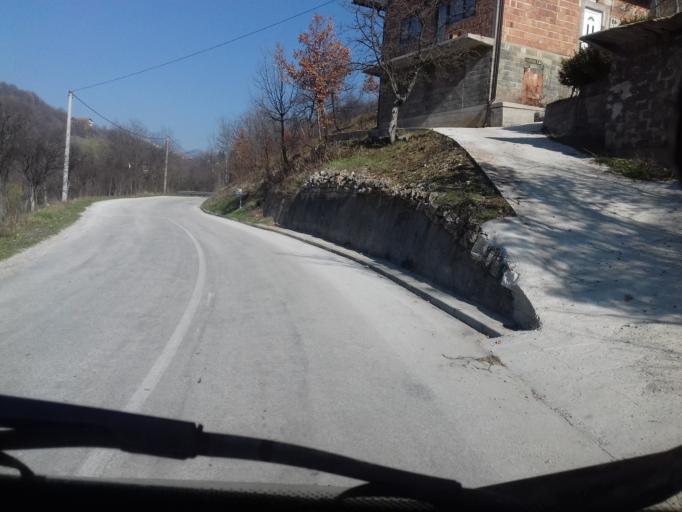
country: BA
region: Federation of Bosnia and Herzegovina
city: Lokvine
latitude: 44.2343
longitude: 17.8275
